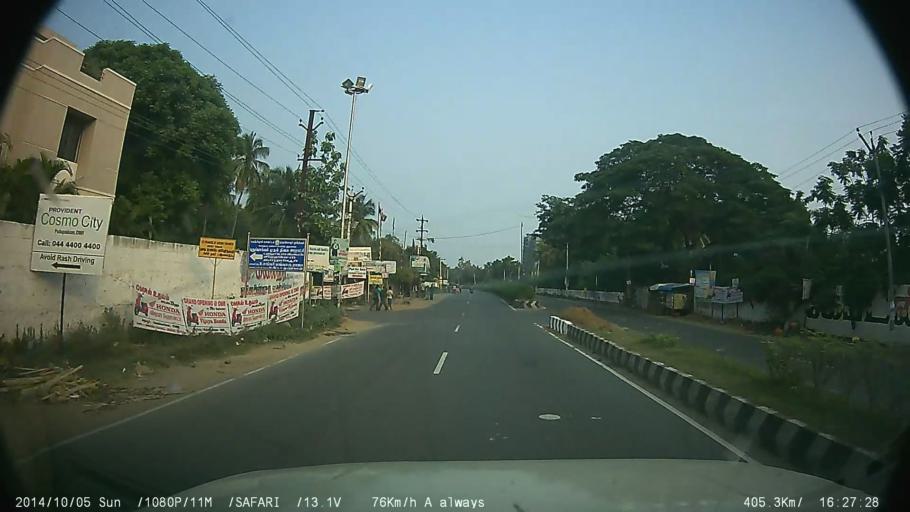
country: IN
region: Tamil Nadu
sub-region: Kancheepuram
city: Vengavasal
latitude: 12.8001
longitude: 80.1974
